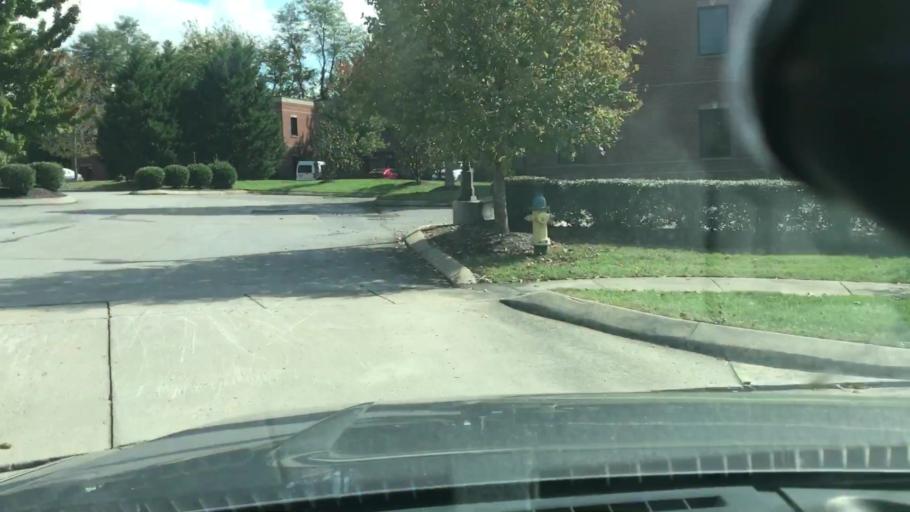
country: US
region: Tennessee
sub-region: Williamson County
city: Franklin
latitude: 35.9391
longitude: -86.8328
